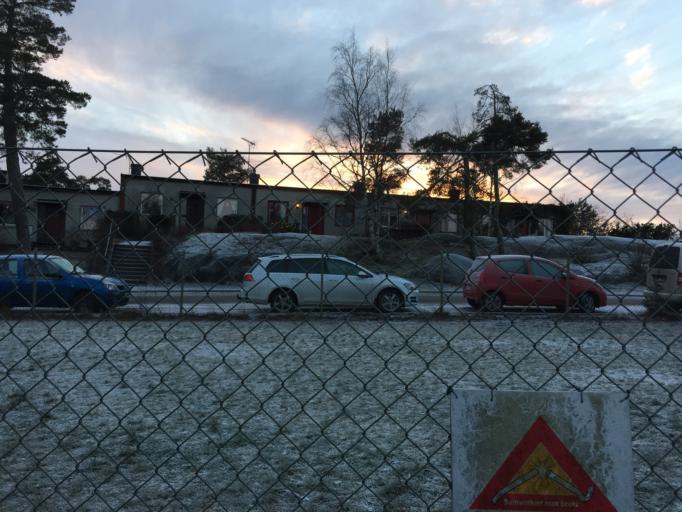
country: SE
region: Stockholm
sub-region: Salems Kommun
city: Ronninge
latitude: 59.1861
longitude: 17.7415
